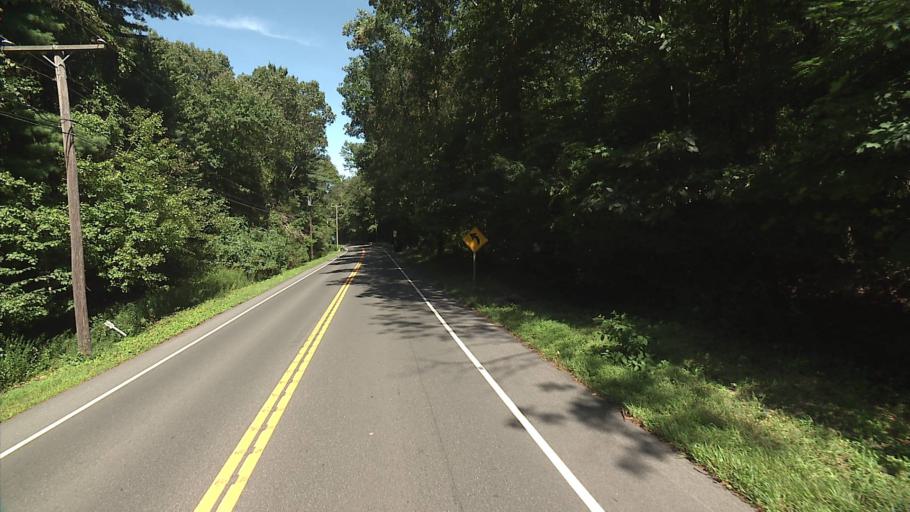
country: US
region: Connecticut
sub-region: New Haven County
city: Seymour
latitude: 41.3748
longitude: -73.1299
